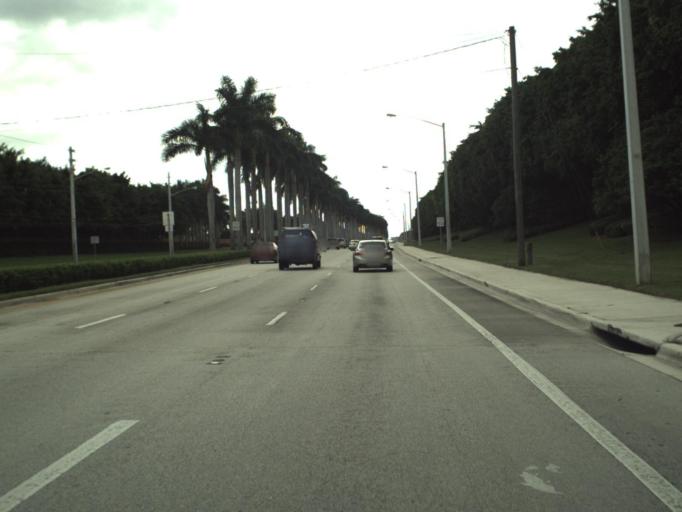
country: US
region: Florida
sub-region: Palm Beach County
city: Wellington
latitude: 26.6506
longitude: -80.2023
